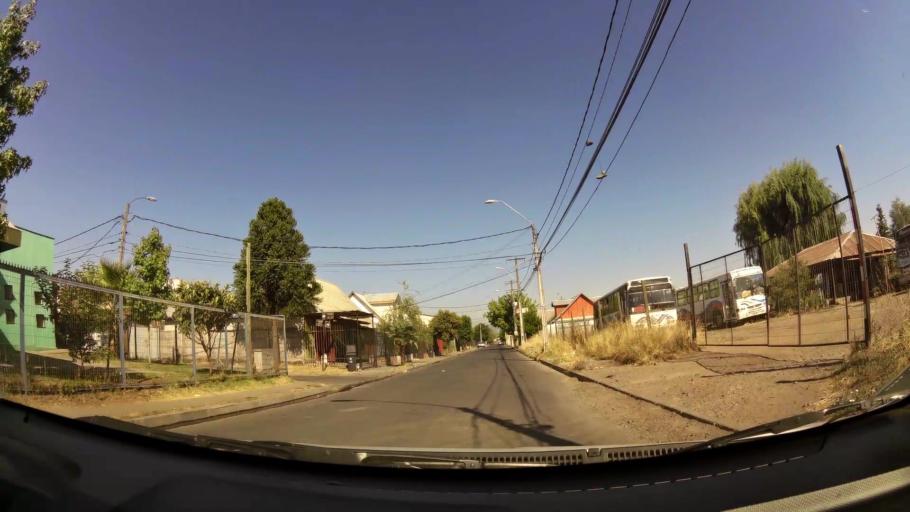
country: CL
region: Maule
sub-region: Provincia de Curico
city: Curico
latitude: -34.9812
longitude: -71.2579
